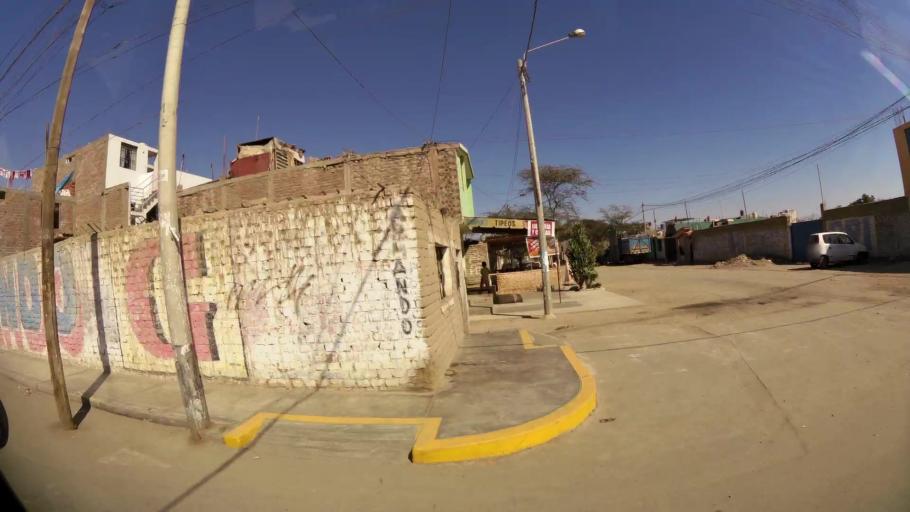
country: PE
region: Ica
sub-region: Provincia de Ica
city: La Tinguina
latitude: -14.0345
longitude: -75.7017
